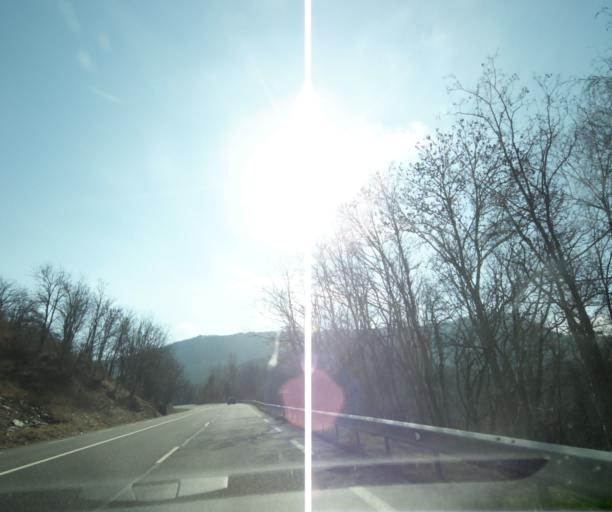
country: FR
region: Languedoc-Roussillon
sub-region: Departement de la Lozere
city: Mende
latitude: 44.5366
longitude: 3.5668
